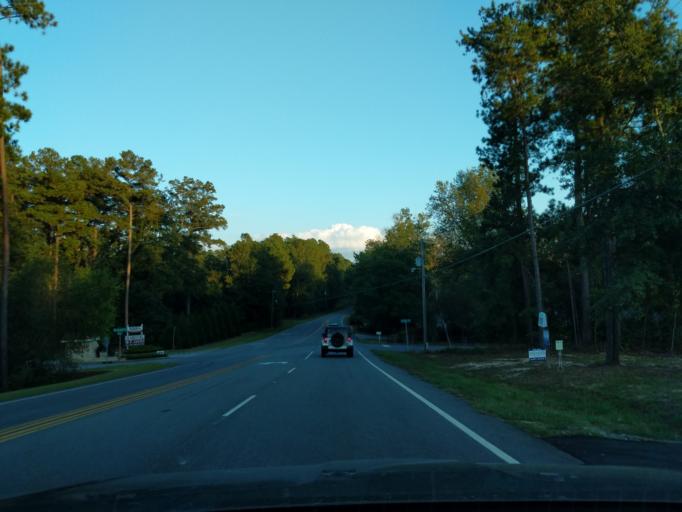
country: US
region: South Carolina
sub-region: Aiken County
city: Burnettown
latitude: 33.5294
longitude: -81.8569
